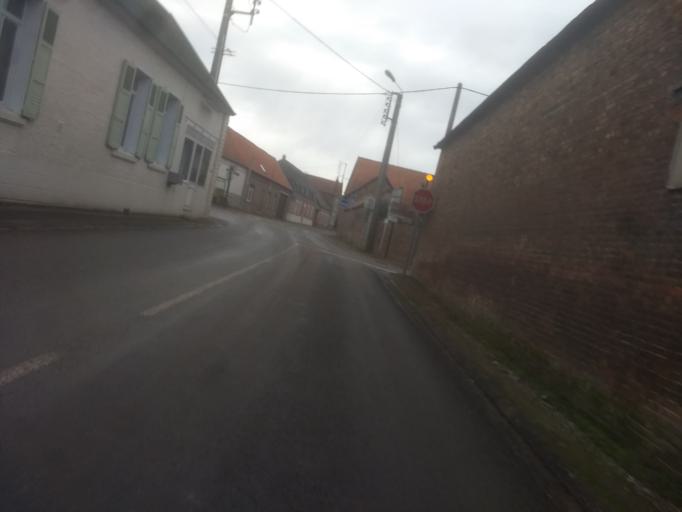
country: FR
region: Nord-Pas-de-Calais
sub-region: Departement du Pas-de-Calais
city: Riviere
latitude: 50.2338
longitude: 2.6972
